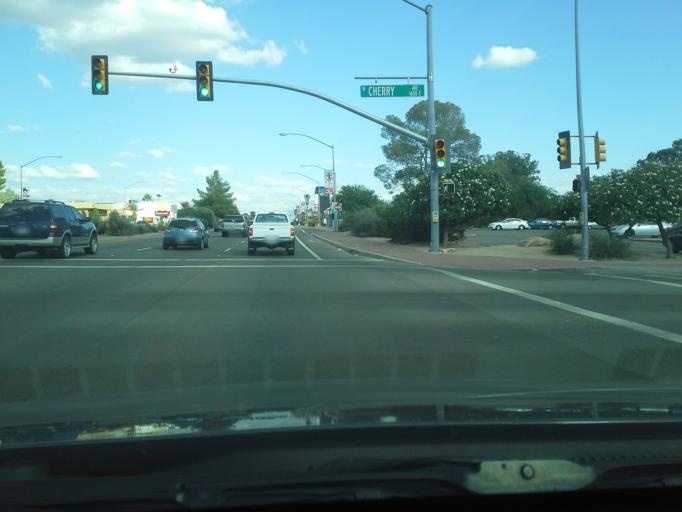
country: US
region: Arizona
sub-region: Pima County
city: Tucson
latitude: 32.2359
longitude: -110.9483
